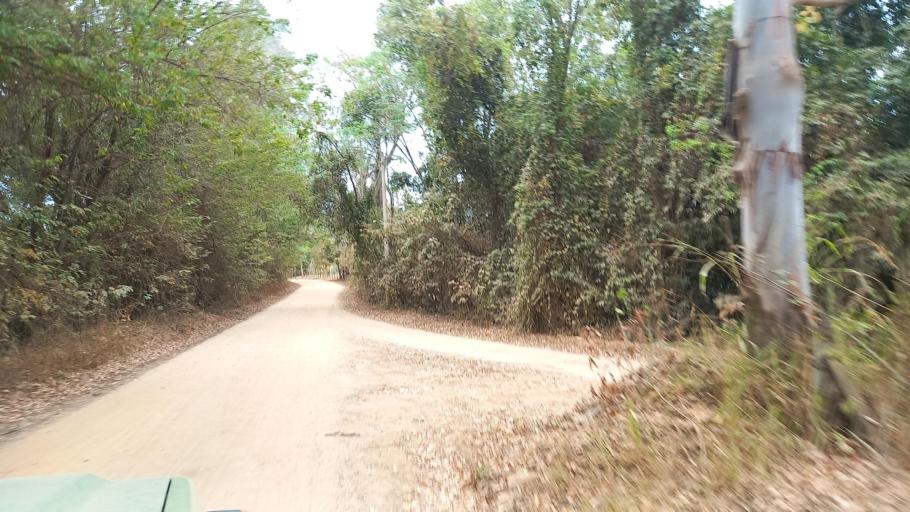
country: BR
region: Sao Paulo
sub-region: Moji-Guacu
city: Mogi-Gaucu
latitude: -22.3068
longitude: -46.8342
